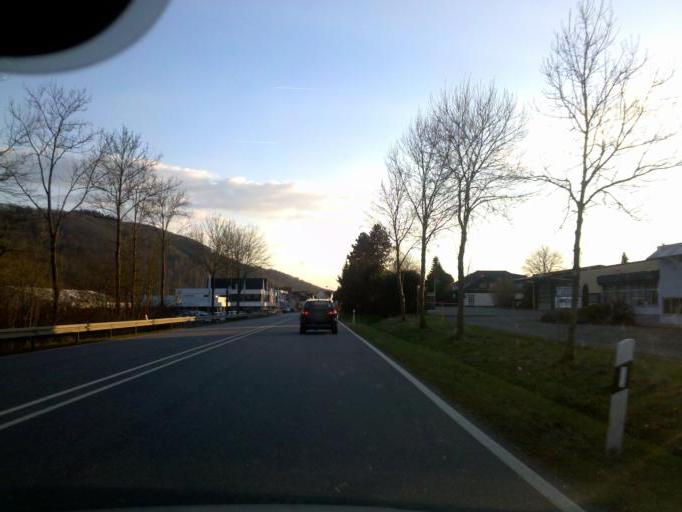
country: DE
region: Hesse
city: Dillenburg
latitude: 50.7789
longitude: 8.3094
